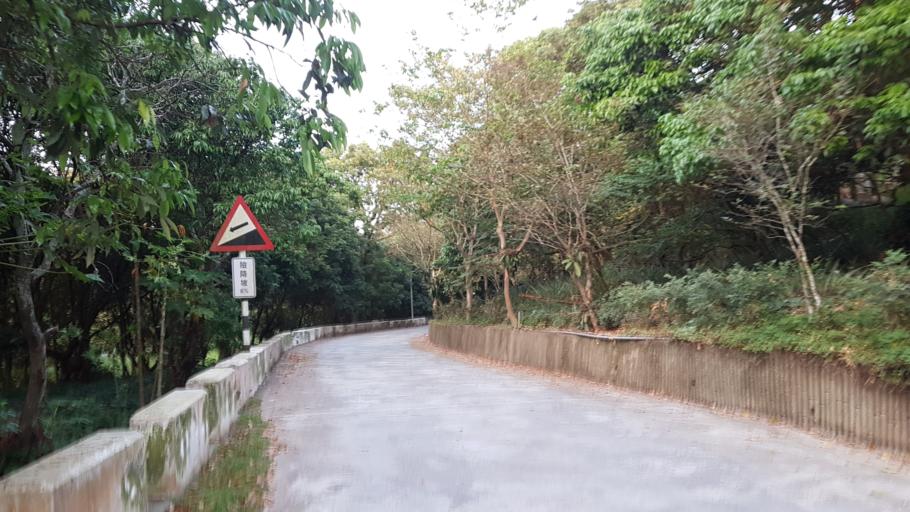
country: TW
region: Taiwan
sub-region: Chiayi
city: Jiayi Shi
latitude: 23.3593
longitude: 120.4677
